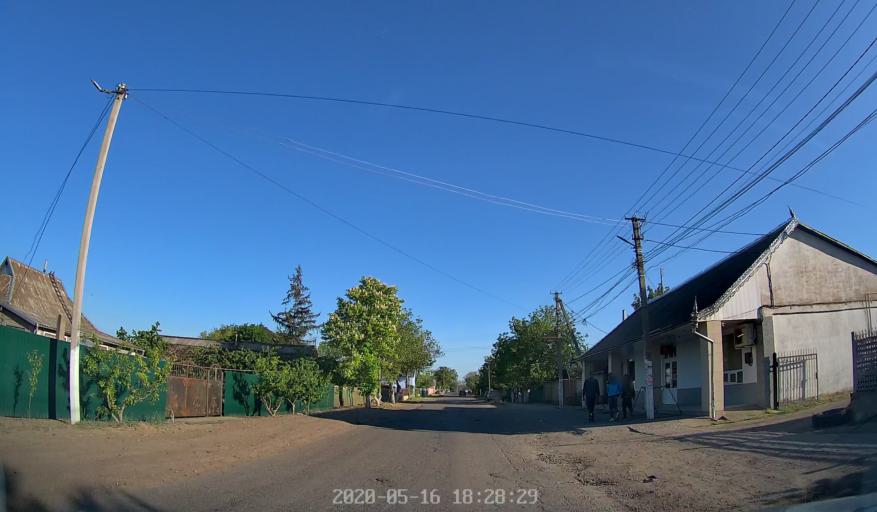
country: MD
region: Telenesti
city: Dnestrovsc
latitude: 46.5394
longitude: 30.0144
